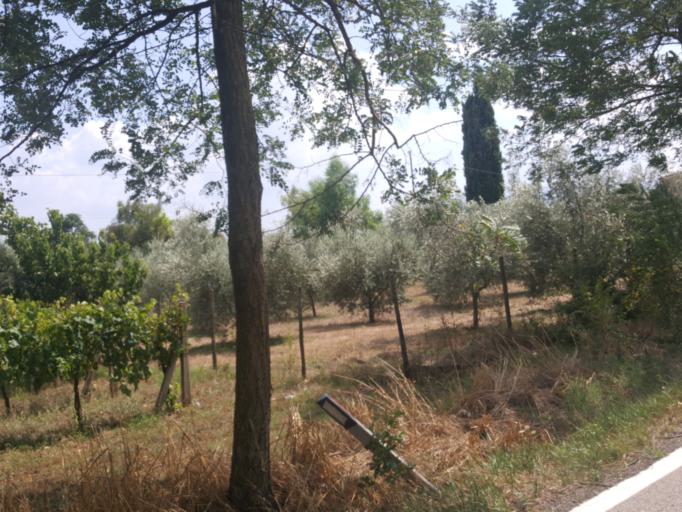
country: IT
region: Latium
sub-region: Provincia di Frosinone
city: Aquino
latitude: 41.5015
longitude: 13.6831
